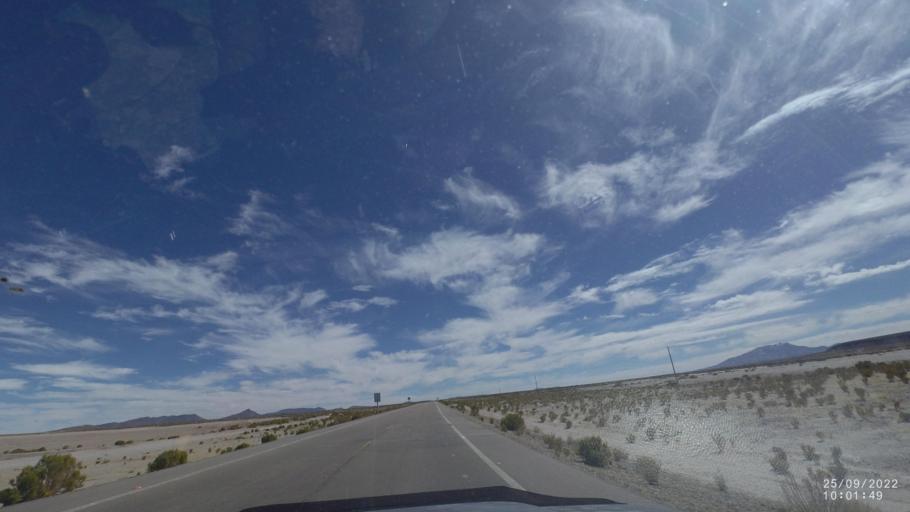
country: BO
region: Potosi
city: Colchani
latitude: -20.2481
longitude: -66.9561
